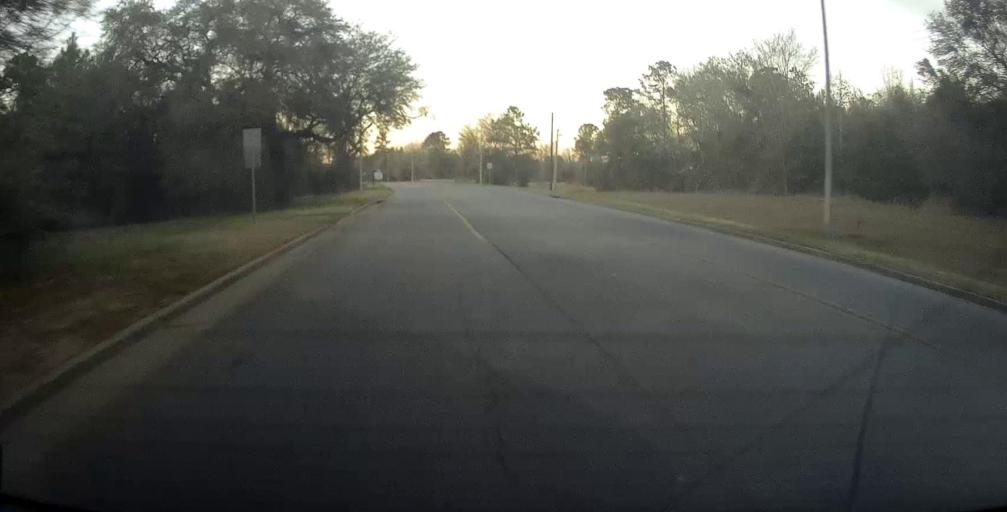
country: US
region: Georgia
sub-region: Dougherty County
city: Albany
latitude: 31.5382
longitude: -84.1364
